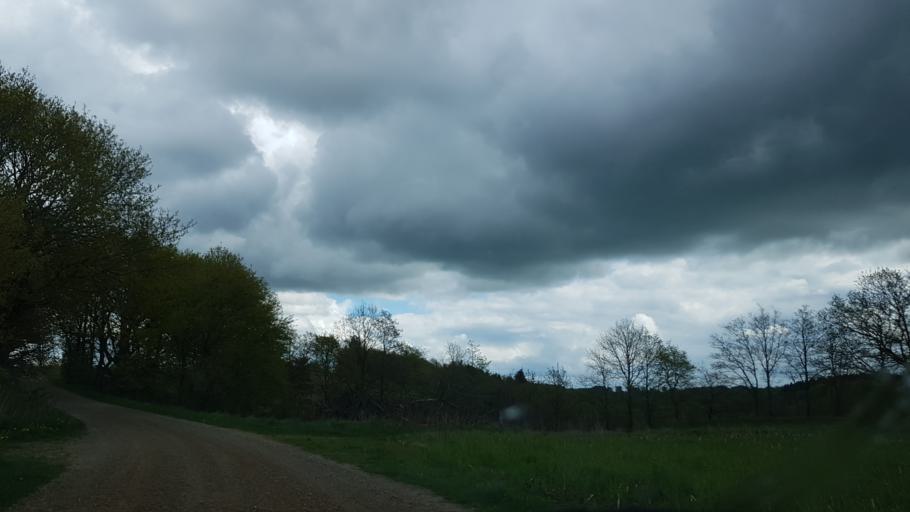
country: DK
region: South Denmark
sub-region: Haderslev Kommune
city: Vojens
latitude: 55.2400
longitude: 9.3288
